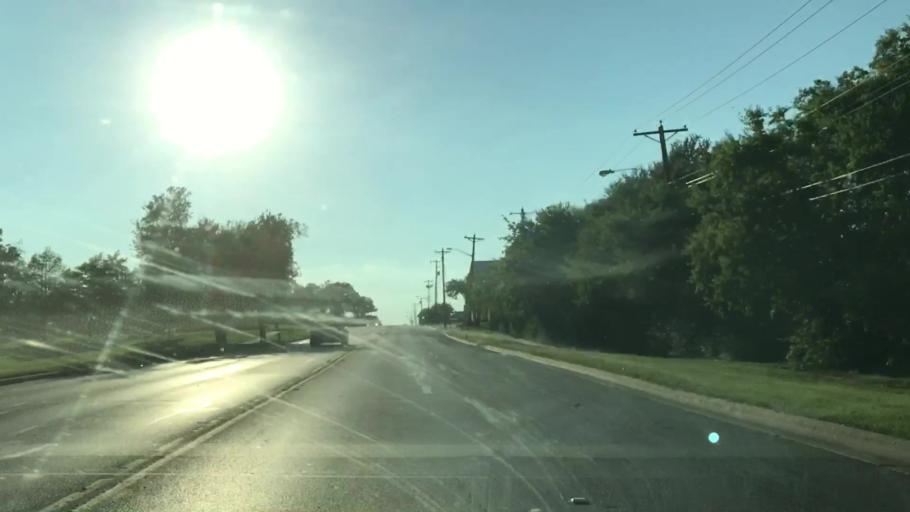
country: US
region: Texas
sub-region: Denton County
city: Denton
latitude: 33.2157
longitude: -97.1144
